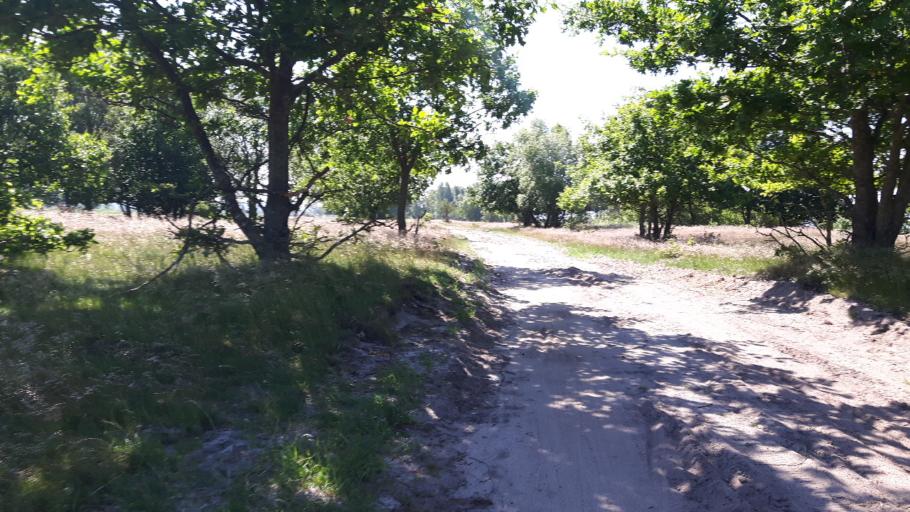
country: PL
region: Pomeranian Voivodeship
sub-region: Powiat slupski
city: Smoldzino
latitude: 54.6732
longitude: 17.1585
